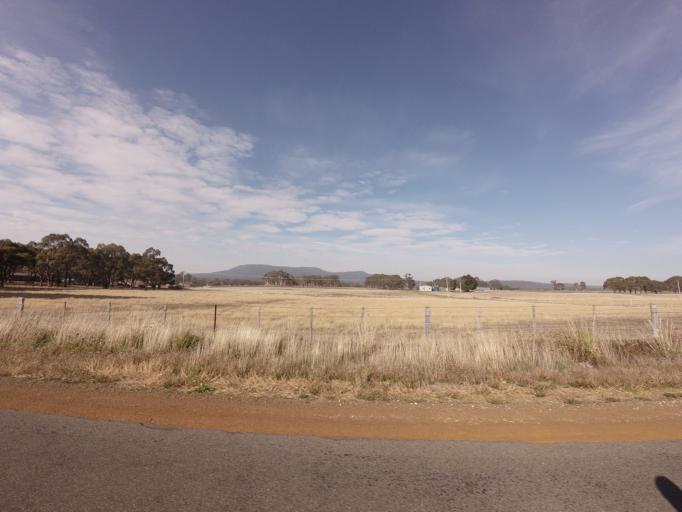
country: AU
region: Tasmania
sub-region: Sorell
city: Sorell
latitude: -42.4474
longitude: 147.4632
